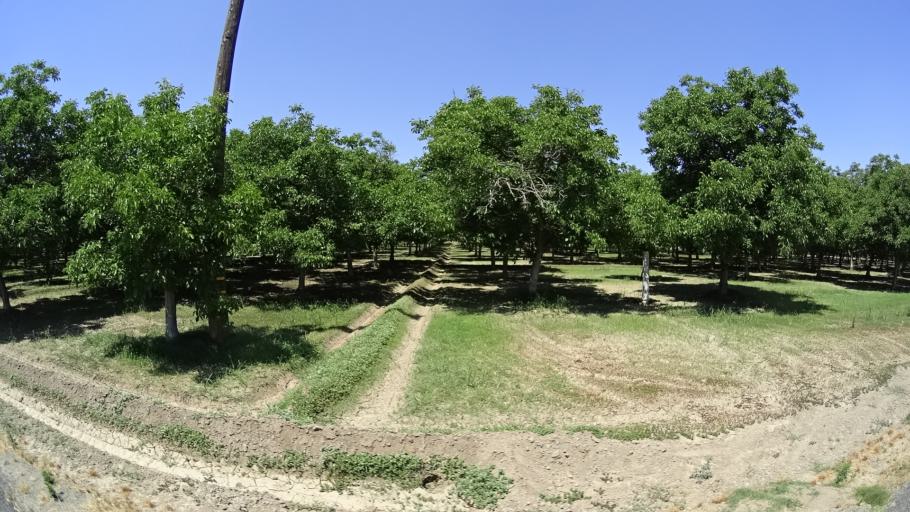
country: US
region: California
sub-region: Fresno County
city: Laton
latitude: 36.4158
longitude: -119.6593
